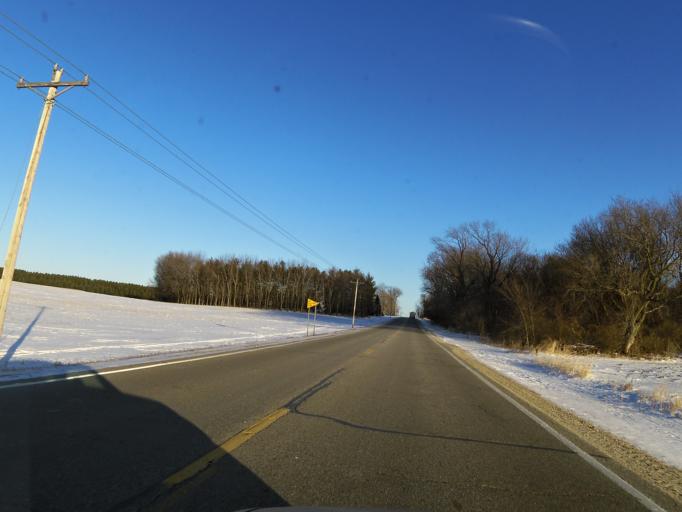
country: US
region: Minnesota
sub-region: Rice County
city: Northfield
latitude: 44.5438
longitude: -93.1782
